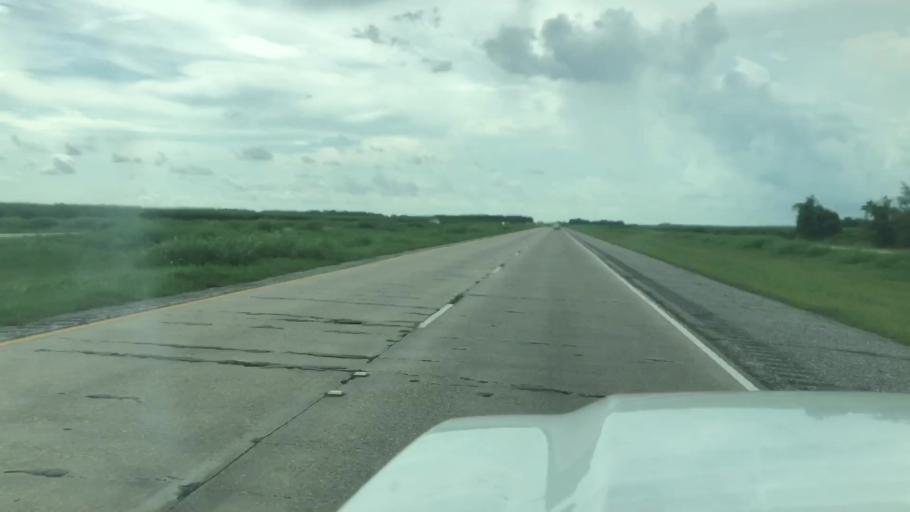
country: US
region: Louisiana
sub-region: Saint Mary Parish
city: Baldwin
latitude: 29.8472
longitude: -91.5895
